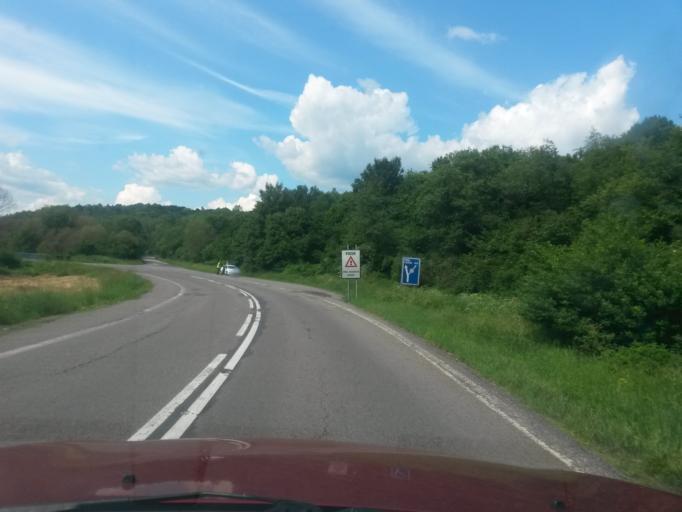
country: UA
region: Zakarpattia
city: Velykyi Bereznyi
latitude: 48.9140
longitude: 22.3722
